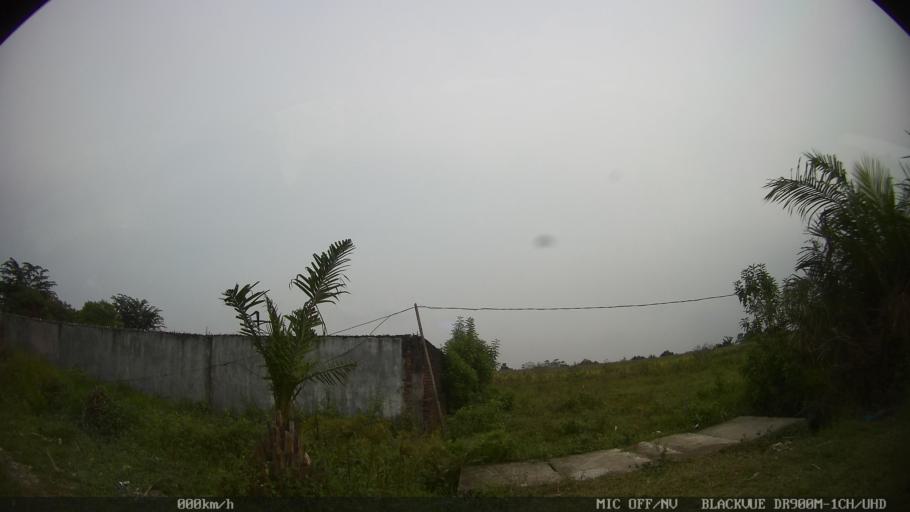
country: ID
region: North Sumatra
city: Medan
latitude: 3.5733
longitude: 98.7454
